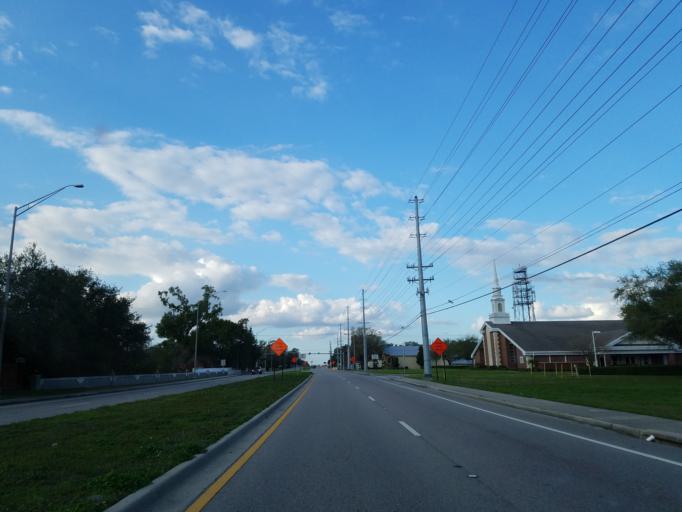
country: US
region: Florida
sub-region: Polk County
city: Lakeland Highlands
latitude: 27.9583
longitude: -81.9236
